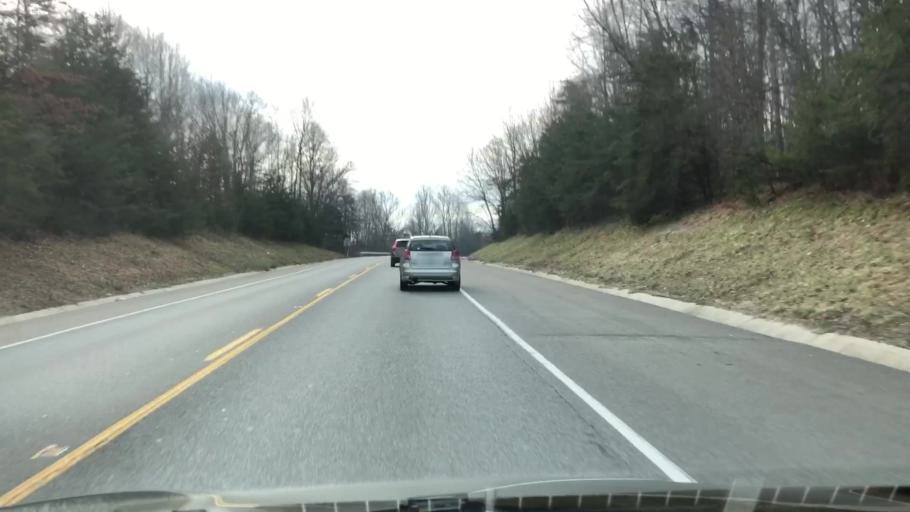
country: US
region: Virginia
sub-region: City of Lynchburg
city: West Lynchburg
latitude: 37.4238
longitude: -79.2323
